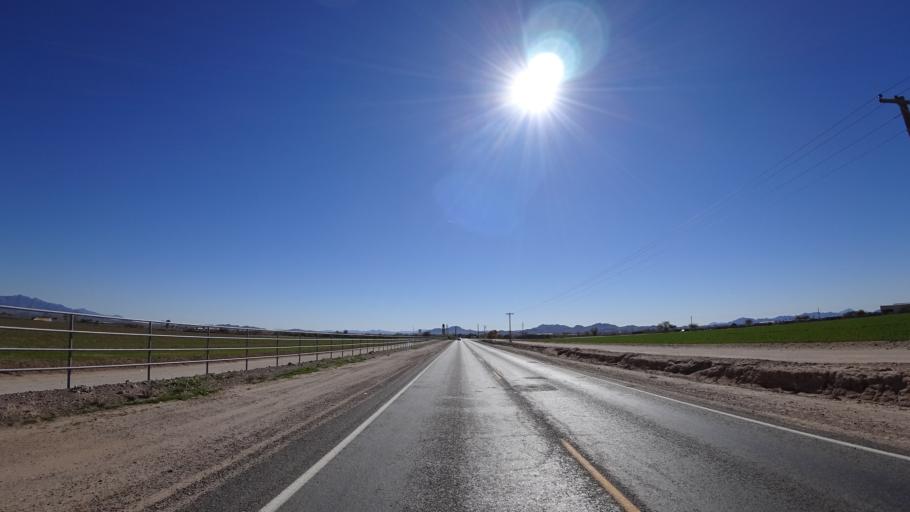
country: US
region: Arizona
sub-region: Maricopa County
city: Buckeye
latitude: 33.3942
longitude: -112.5214
